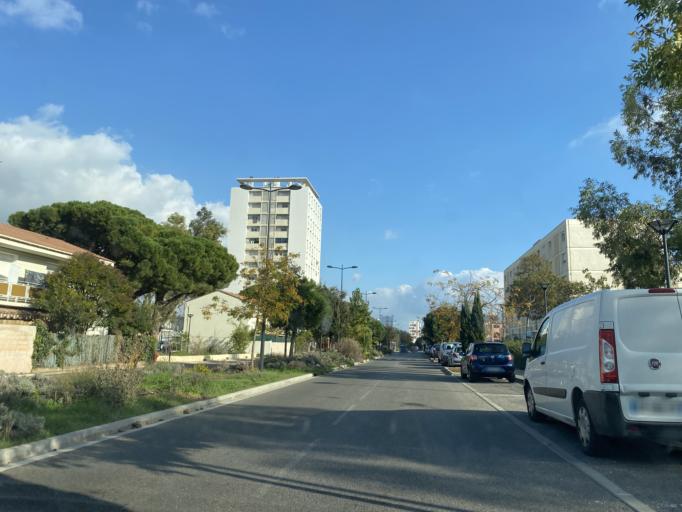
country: FR
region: Provence-Alpes-Cote d'Azur
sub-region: Departement du Var
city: Six-Fours-les-Plages
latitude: 43.1103
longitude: 5.8625
